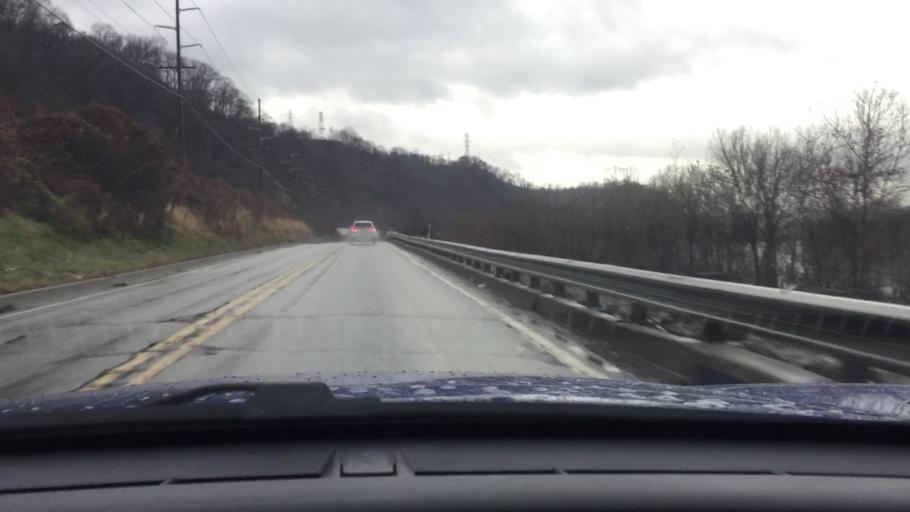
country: US
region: Pennsylvania
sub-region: Allegheny County
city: West Homestead
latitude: 40.3975
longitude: -79.9471
